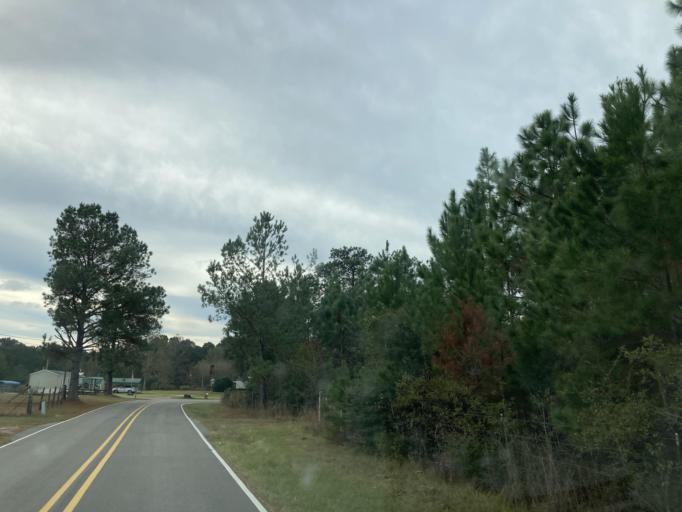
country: US
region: Mississippi
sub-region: Lamar County
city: Purvis
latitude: 31.1606
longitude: -89.4607
